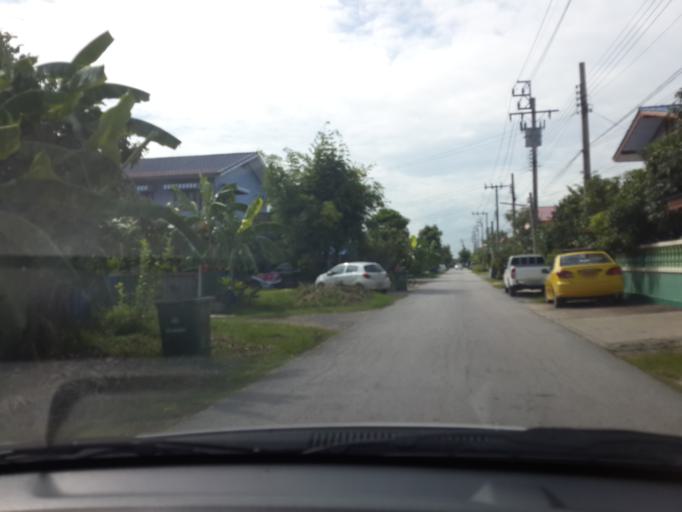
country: TH
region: Bangkok
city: Khlong Sam Wa
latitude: 13.8458
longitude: 100.7842
